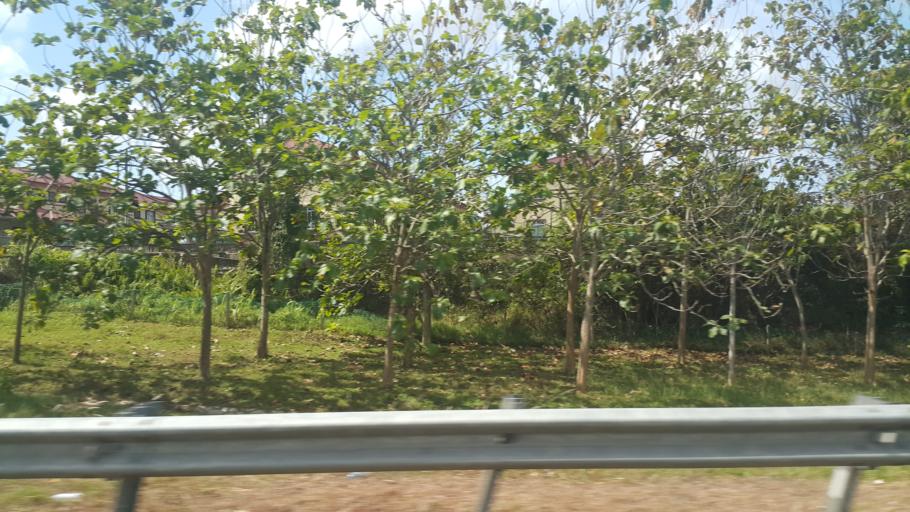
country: MY
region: Johor
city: Bakri
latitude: 2.1419
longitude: 102.7136
